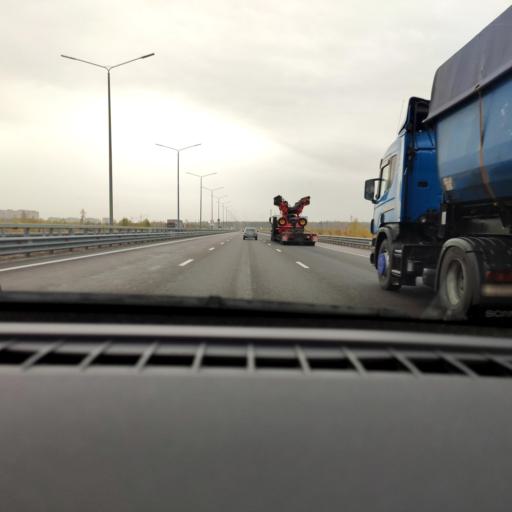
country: RU
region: Voronezj
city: Somovo
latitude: 51.7564
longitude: 39.3068
